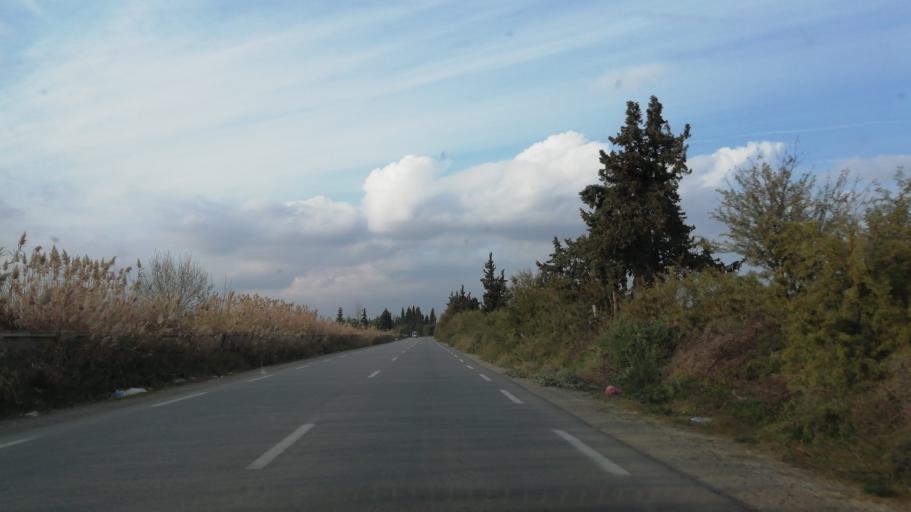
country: DZ
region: Mascara
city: Mascara
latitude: 35.6291
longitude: 0.0413
